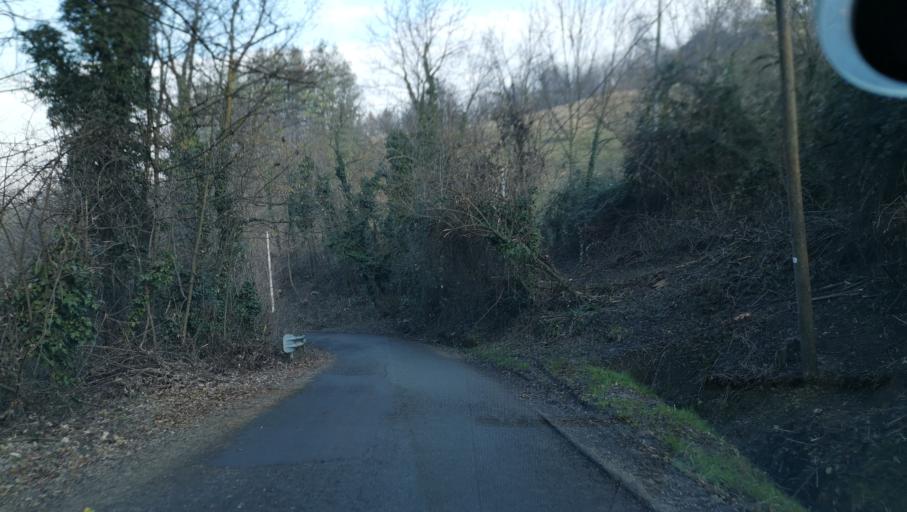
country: IT
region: Piedmont
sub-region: Provincia di Torino
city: Gassino Torinese
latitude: 45.1161
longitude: 7.8348
